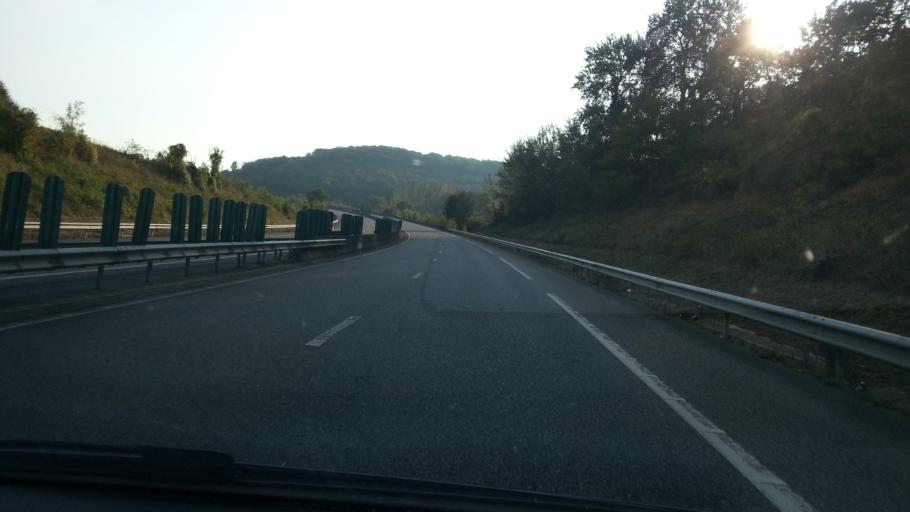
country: FR
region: Picardie
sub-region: Departement de l'Oise
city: Cambronne-les-Ribecourt
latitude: 49.5148
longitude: 2.8941
